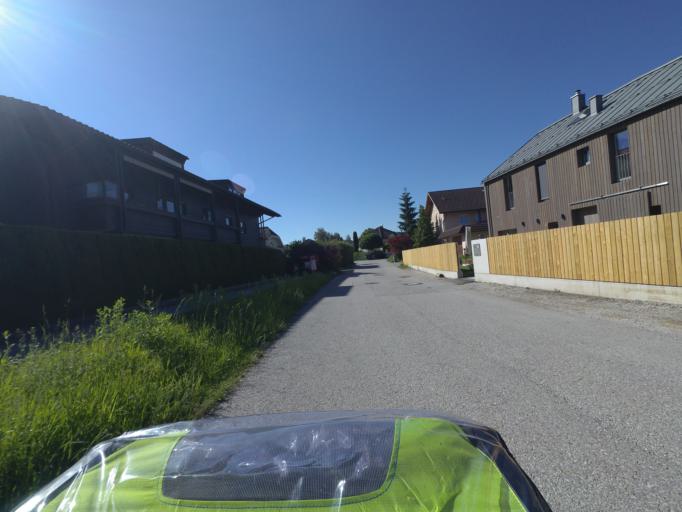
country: AT
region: Salzburg
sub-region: Politischer Bezirk Salzburg-Umgebung
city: Anif
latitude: 47.7482
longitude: 13.0587
